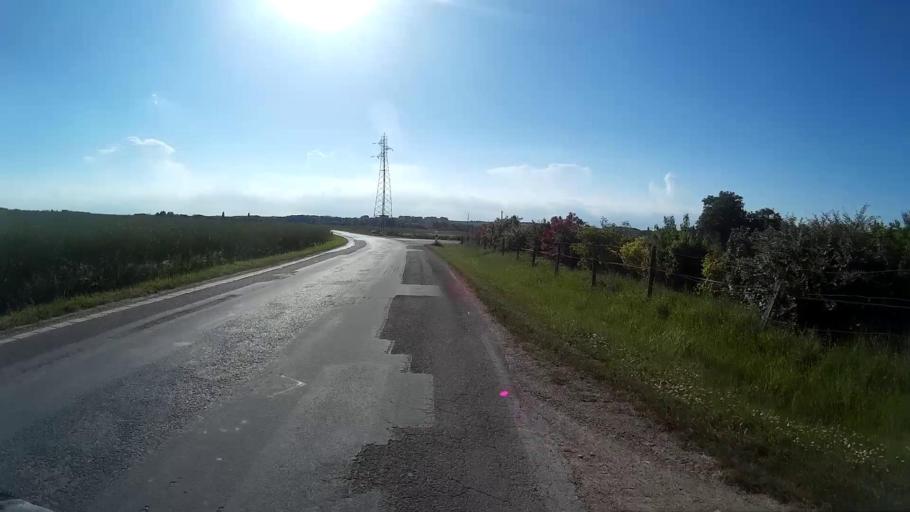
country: FR
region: Centre
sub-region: Departement du Loir-et-Cher
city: Villiers-sur-Loir
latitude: 47.8058
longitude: 0.9729
